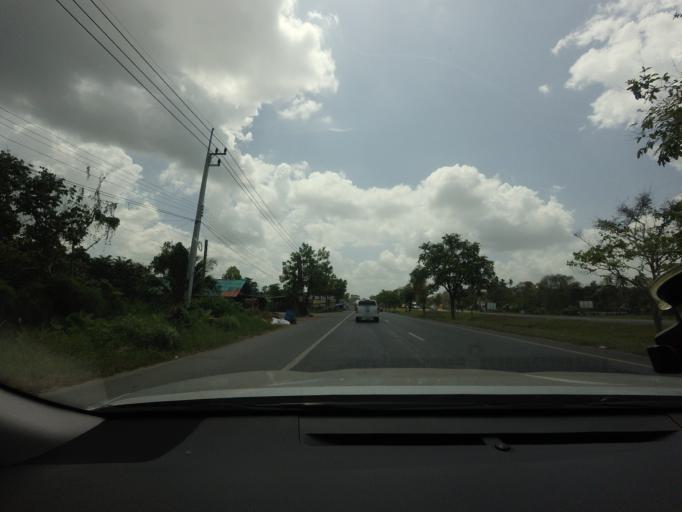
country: TH
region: Nakhon Si Thammarat
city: Nakhon Si Thammarat
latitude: 8.4226
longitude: 99.9215
